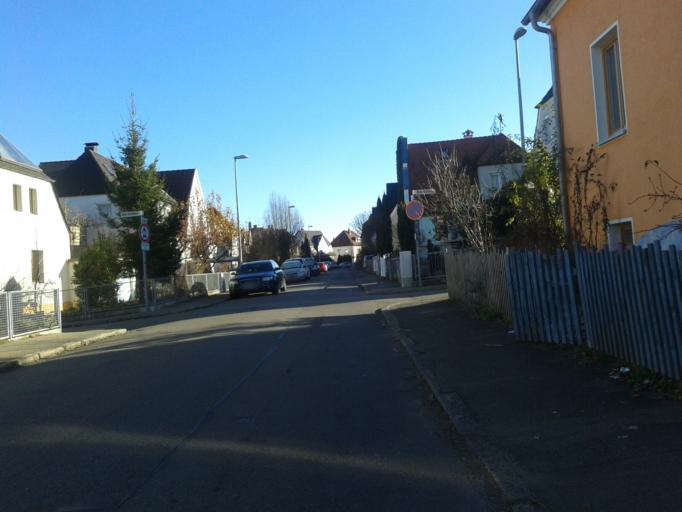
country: DE
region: Baden-Wuerttemberg
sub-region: Tuebingen Region
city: Ulm
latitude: 48.3894
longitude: 9.9697
